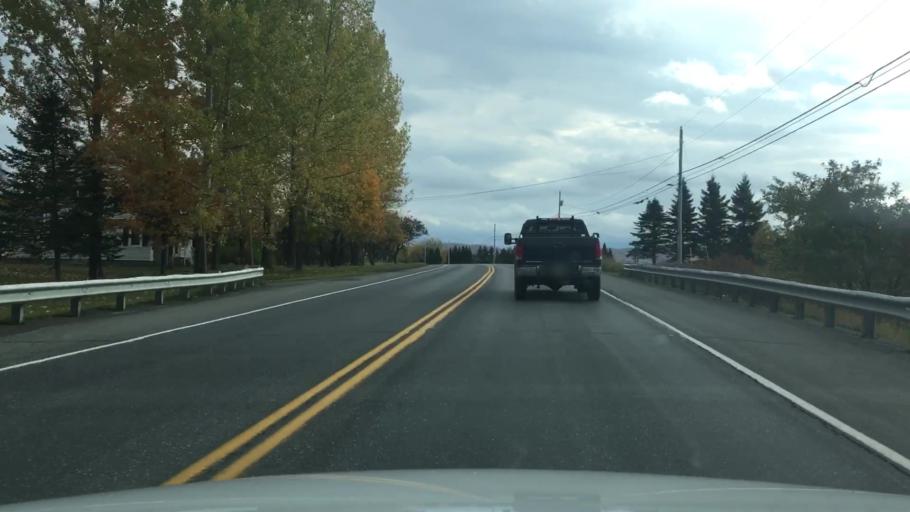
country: US
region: Maine
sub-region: Aroostook County
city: Easton
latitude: 46.5653
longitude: -67.9481
